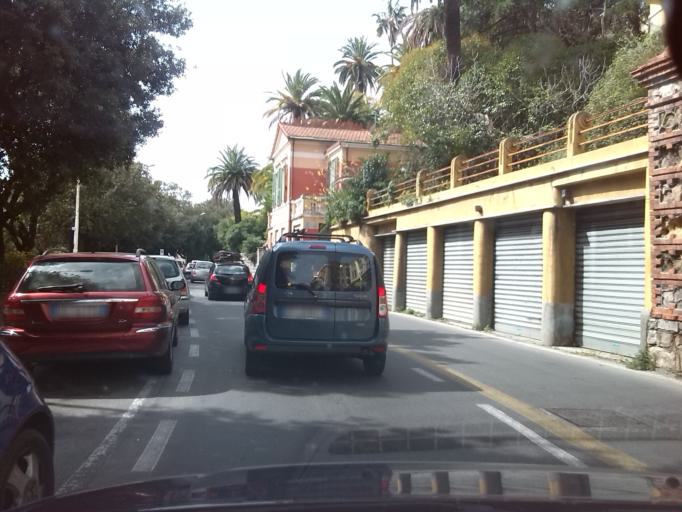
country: IT
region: Liguria
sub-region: Provincia di Imperia
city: Imperia
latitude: 43.8813
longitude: 8.0188
